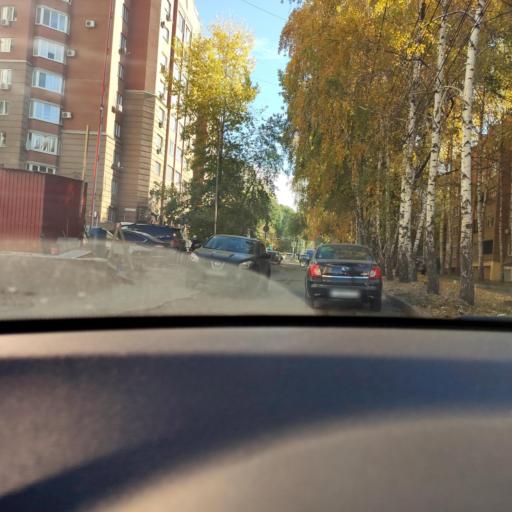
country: RU
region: Samara
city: Samara
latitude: 53.2150
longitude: 50.1614
